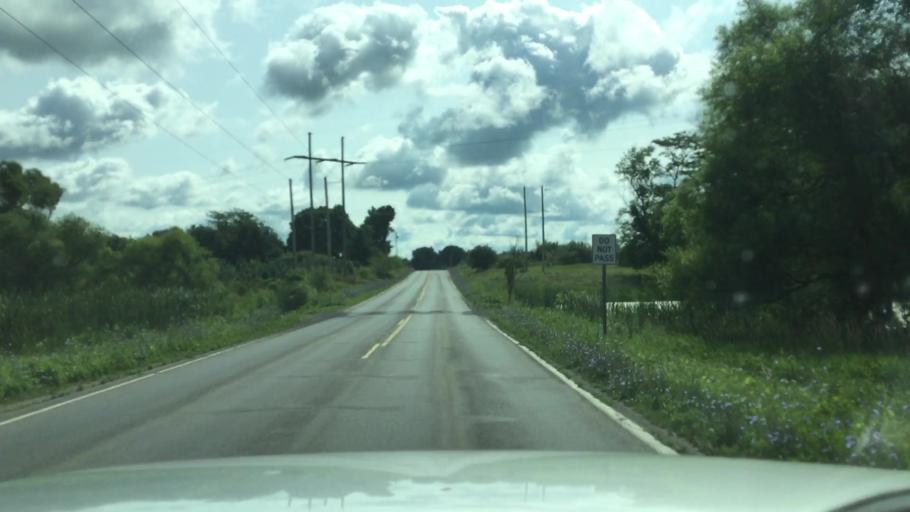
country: US
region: Michigan
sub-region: Montcalm County
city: Greenville
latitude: 43.1924
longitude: -85.2094
